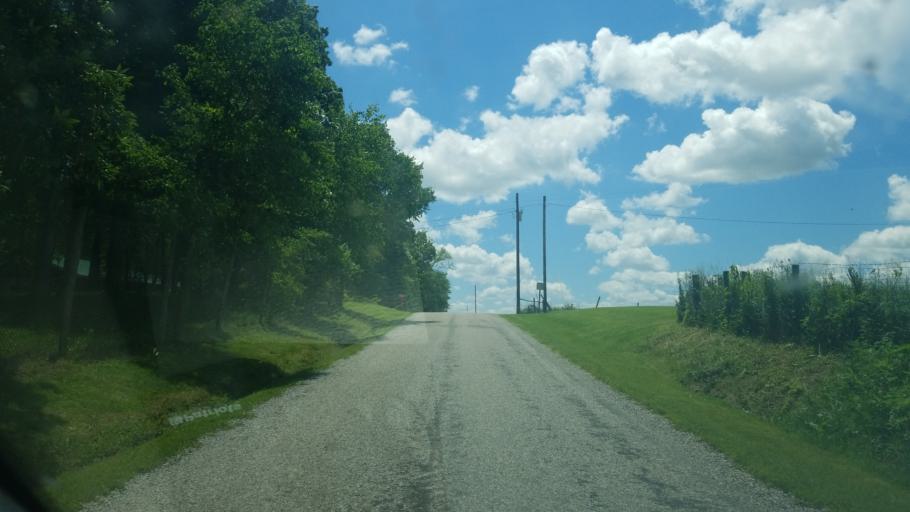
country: US
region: Ohio
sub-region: Ashland County
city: Ashland
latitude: 40.9863
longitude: -82.3266
